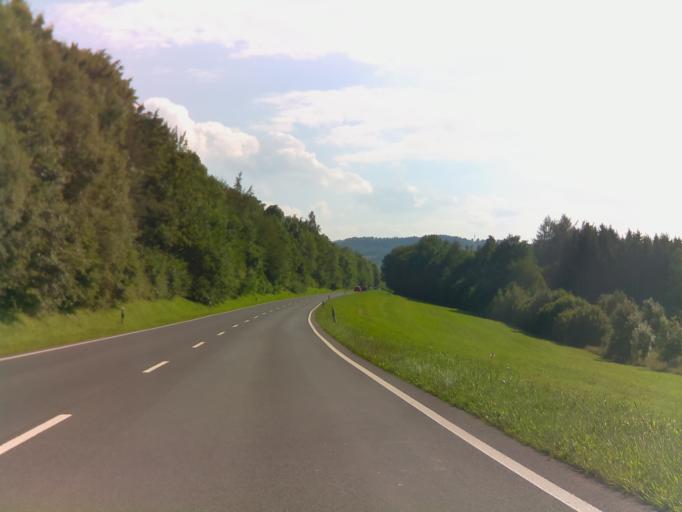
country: DE
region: Bavaria
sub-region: Regierungsbezirk Unterfranken
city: Riedenberg
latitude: 50.3357
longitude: 9.8780
